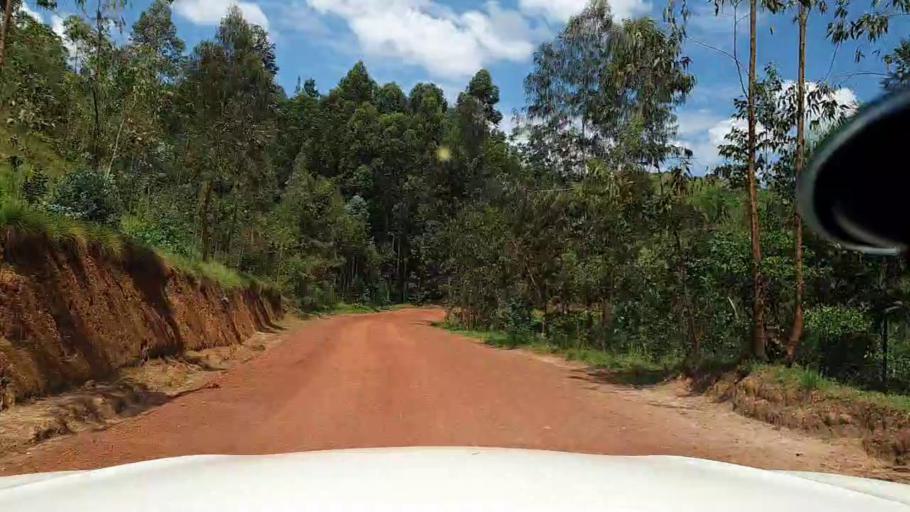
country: RW
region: Northern Province
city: Byumba
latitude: -1.7435
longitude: 29.8628
